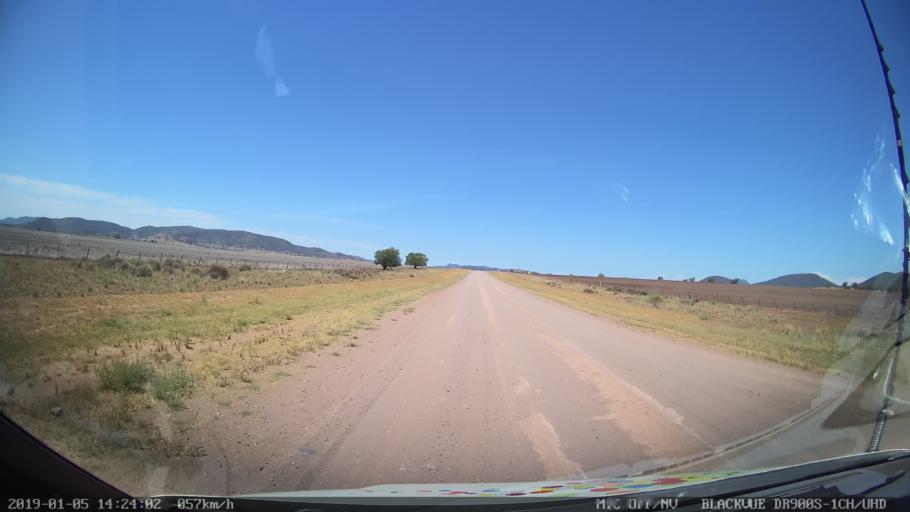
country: AU
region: New South Wales
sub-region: Liverpool Plains
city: Quirindi
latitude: -31.2416
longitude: 150.5365
